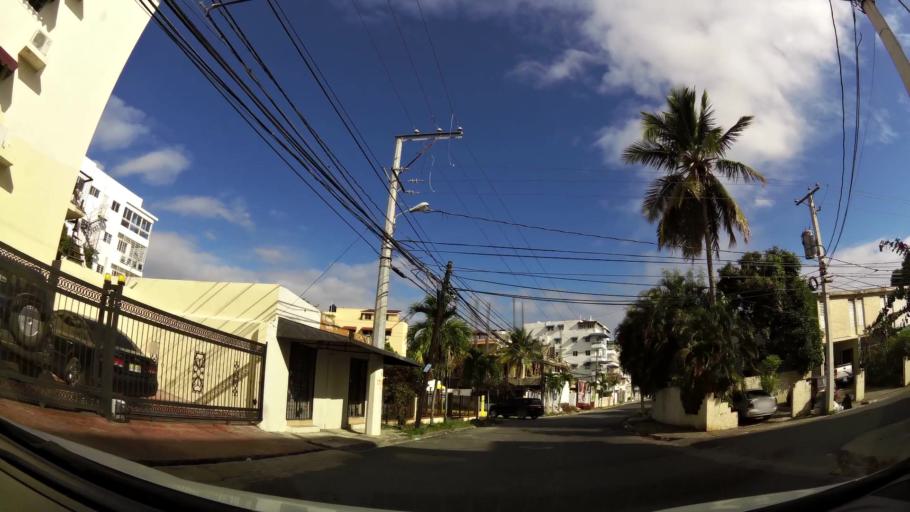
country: DO
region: Nacional
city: Bella Vista
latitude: 18.4642
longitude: -69.9540
